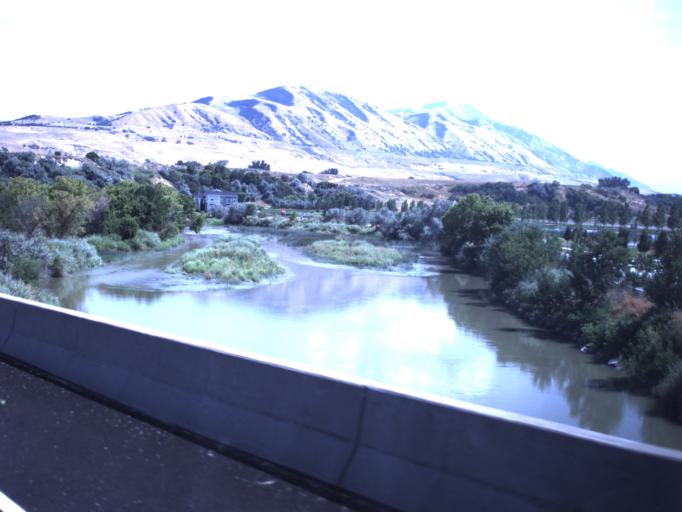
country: US
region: Utah
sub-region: Box Elder County
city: Garland
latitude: 41.7843
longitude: -112.1124
